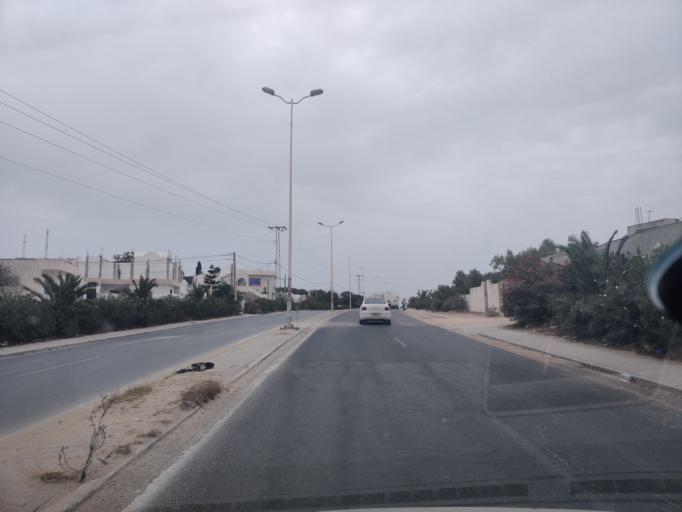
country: TN
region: Nabul
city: Al Hammamat
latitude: 36.4094
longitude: 10.6186
